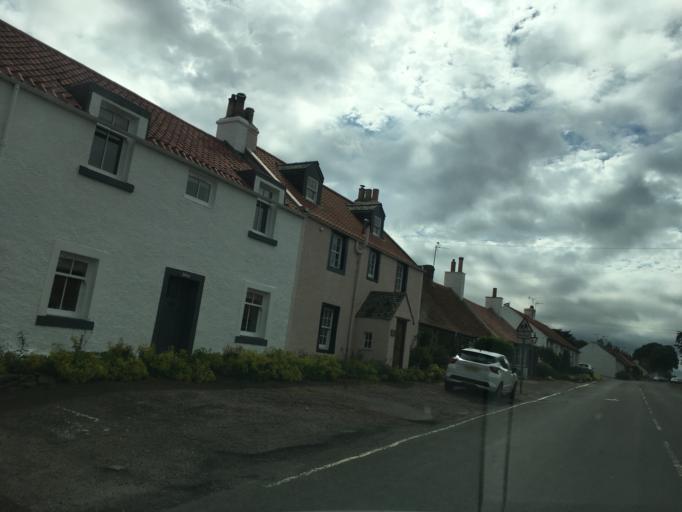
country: GB
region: Scotland
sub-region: East Lothian
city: Haddington
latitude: 55.9869
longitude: -2.7456
